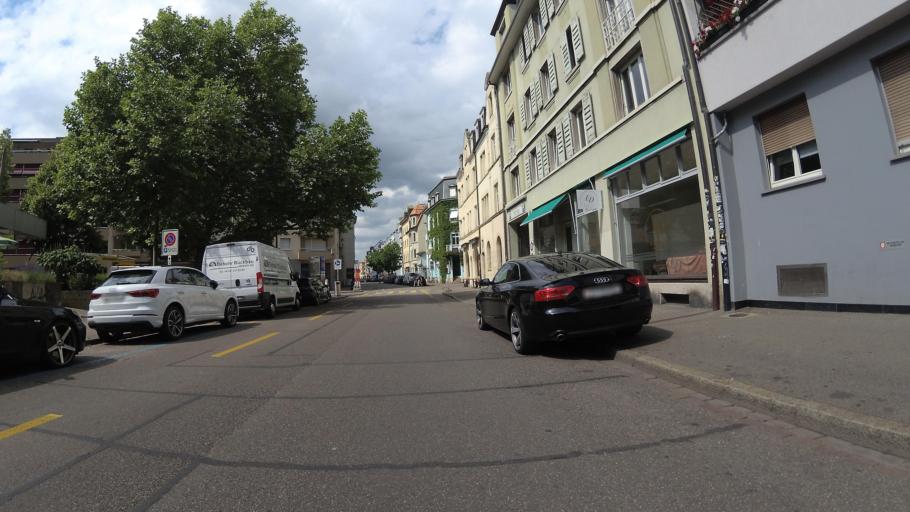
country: CH
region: Basel-City
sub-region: Basel-Stadt
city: Basel
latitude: 47.5651
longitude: 7.5958
